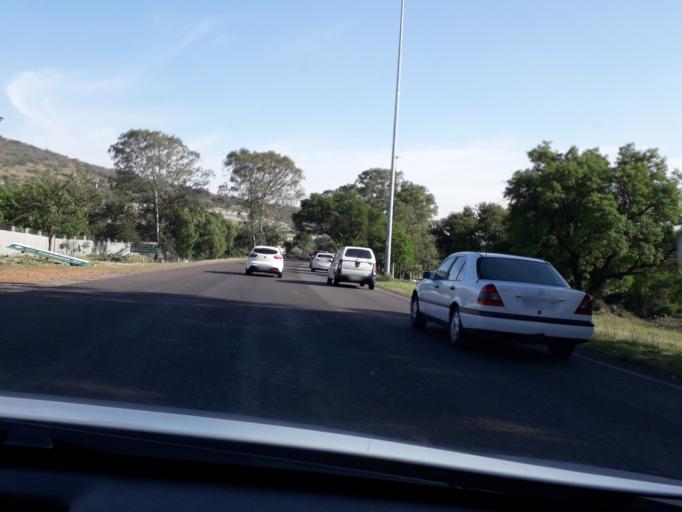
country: ZA
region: Gauteng
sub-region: City of Tshwane Metropolitan Municipality
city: Pretoria
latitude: -25.7835
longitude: 28.1934
